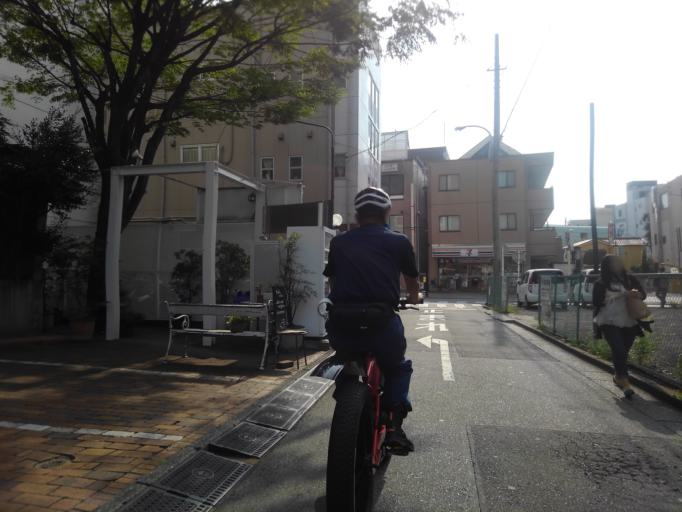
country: JP
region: Kanagawa
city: Minami-rinkan
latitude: 35.4694
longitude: 139.4604
